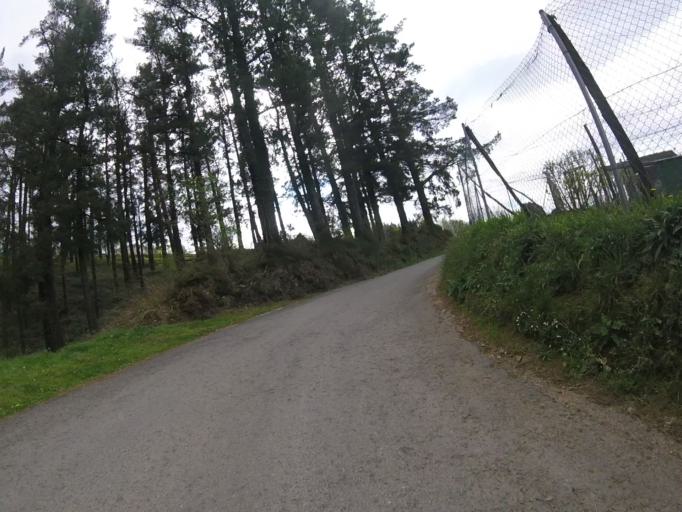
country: ES
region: Basque Country
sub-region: Provincia de Guipuzcoa
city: Aizarnazabal
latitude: 43.2492
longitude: -2.1949
